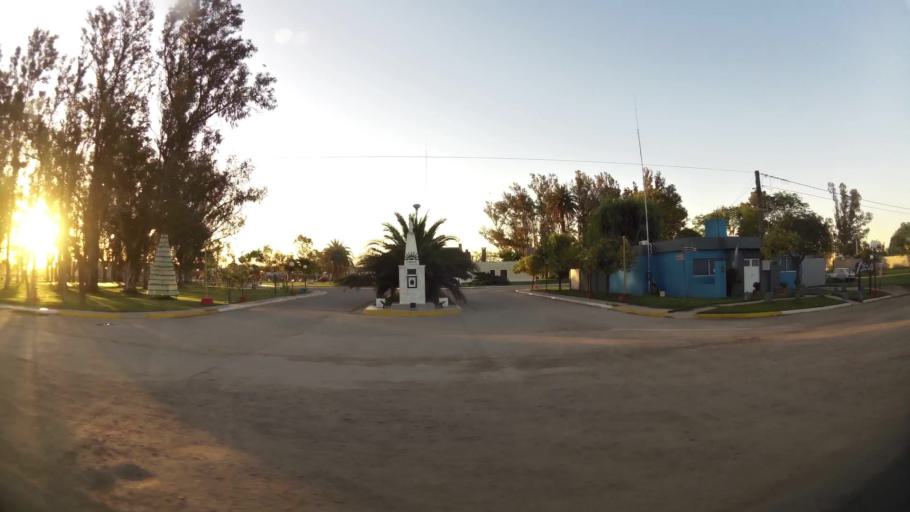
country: AR
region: Cordoba
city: La Playosa
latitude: -32.2030
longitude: -63.1619
